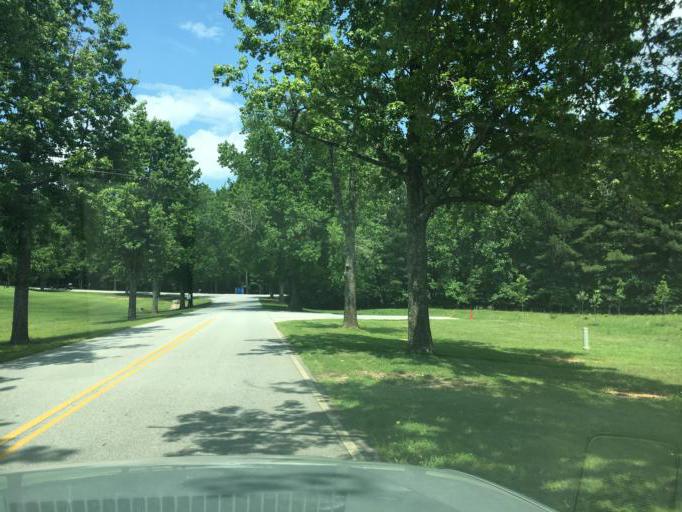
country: US
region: South Carolina
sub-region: Greenville County
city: Greer
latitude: 34.8932
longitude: -82.2127
